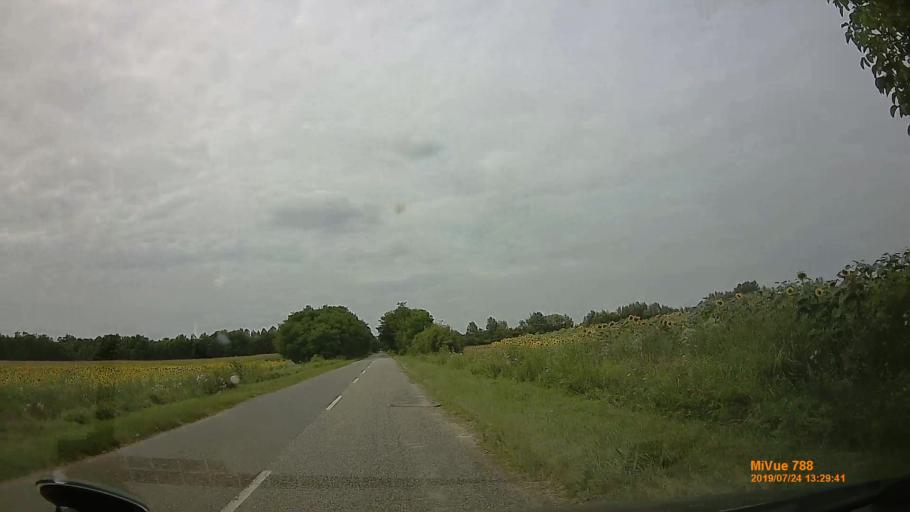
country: HU
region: Szabolcs-Szatmar-Bereg
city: Vasarosnameny
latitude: 48.2275
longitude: 22.3939
